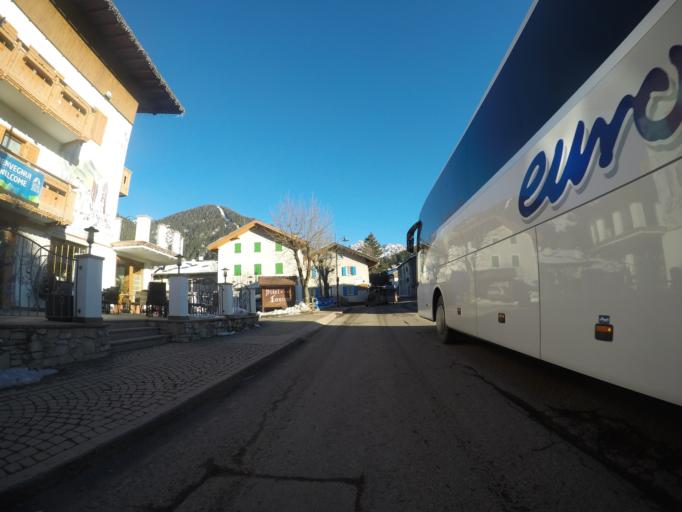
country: IT
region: Trentino-Alto Adige
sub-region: Provincia di Trento
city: Pozza di Fassa
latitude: 46.4303
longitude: 11.6887
